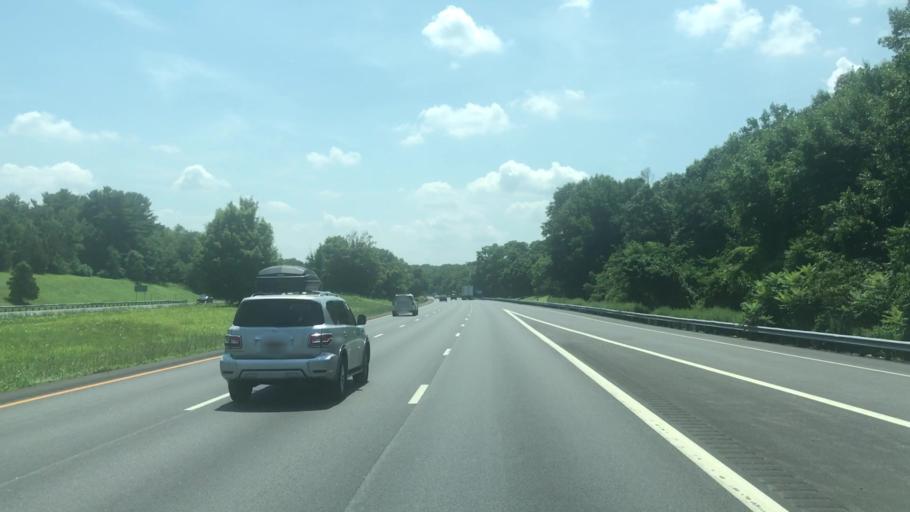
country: US
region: New York
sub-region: Westchester County
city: Bedford Hills
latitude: 41.2291
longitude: -73.6819
